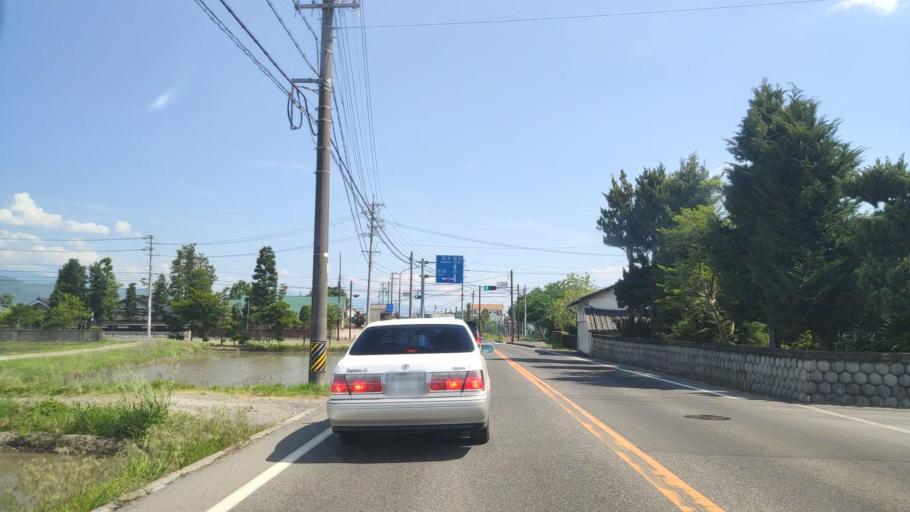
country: JP
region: Nagano
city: Hotaka
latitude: 36.3742
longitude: 137.8728
